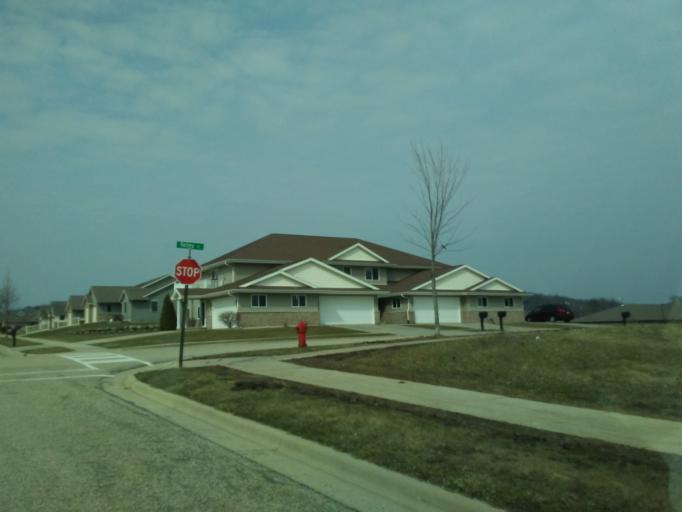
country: US
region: Wisconsin
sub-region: Columbia County
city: Lodi
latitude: 43.3097
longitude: -89.5442
